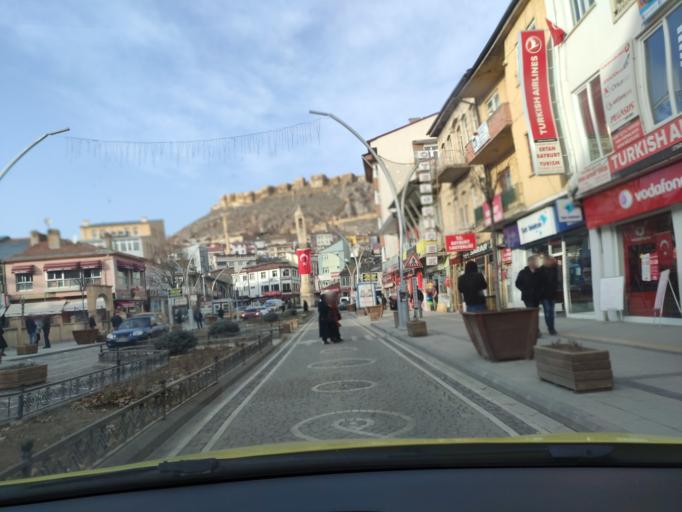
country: TR
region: Bayburt
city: Bayburt
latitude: 40.2596
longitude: 40.2269
